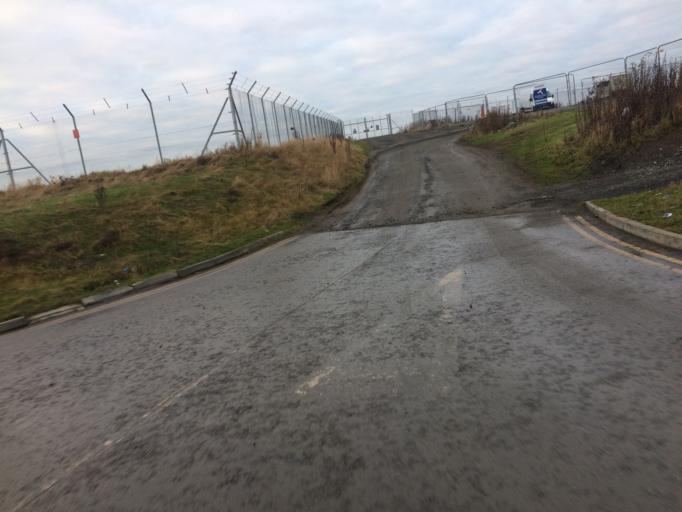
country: GB
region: Scotland
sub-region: Edinburgh
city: Currie
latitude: 55.9408
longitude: -3.3248
